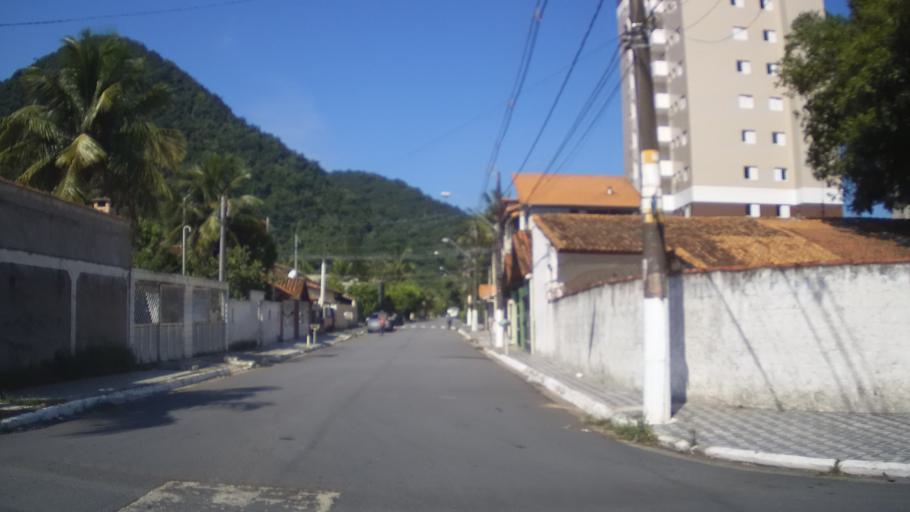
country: BR
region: Sao Paulo
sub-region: Praia Grande
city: Praia Grande
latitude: -24.0040
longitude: -46.4050
